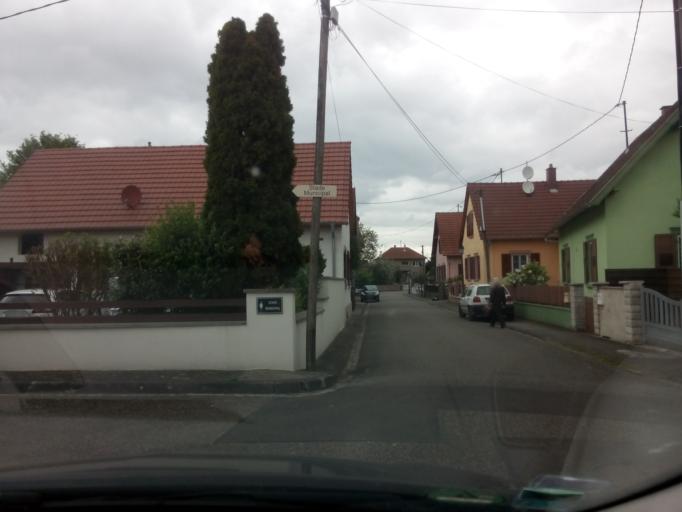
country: DE
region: Baden-Wuerttemberg
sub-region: Karlsruhe Region
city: Greffern
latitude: 48.7976
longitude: 8.0033
